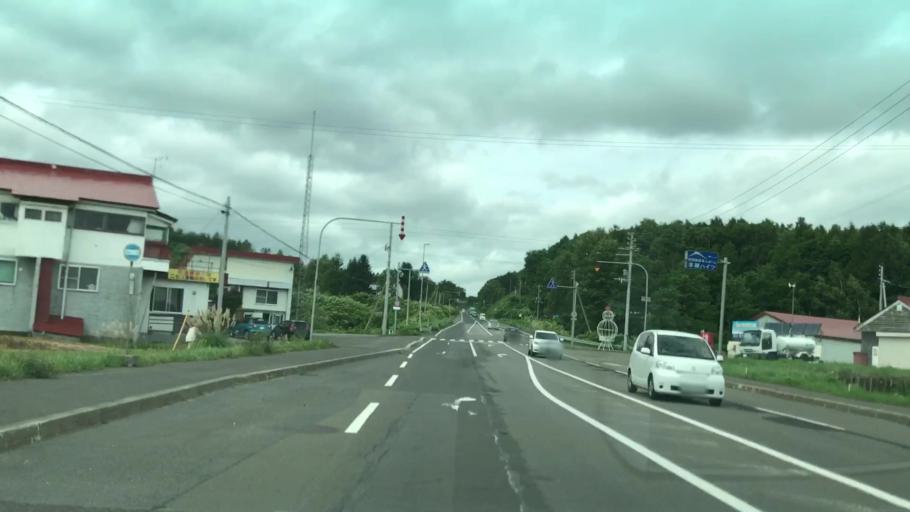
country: JP
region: Hokkaido
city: Niseko Town
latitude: 42.9217
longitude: 140.7389
